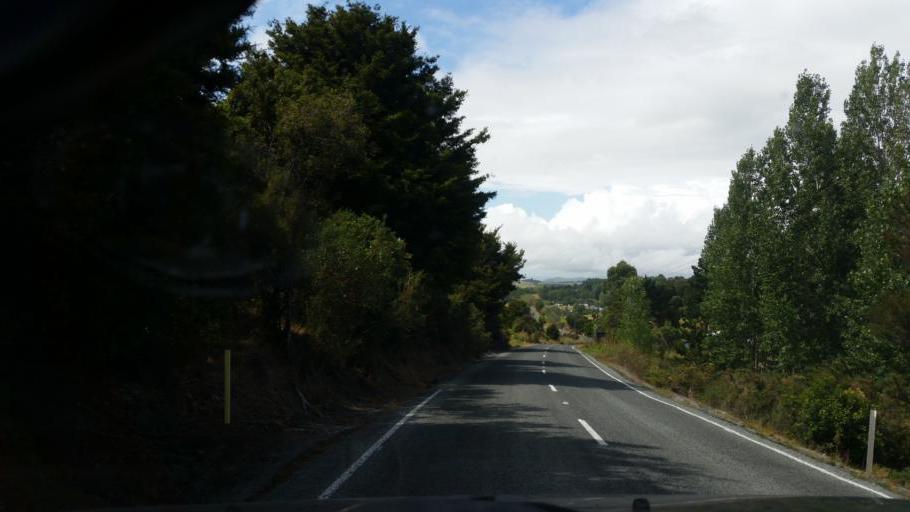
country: NZ
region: Auckland
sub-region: Auckland
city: Wellsford
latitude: -36.1153
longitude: 174.5438
